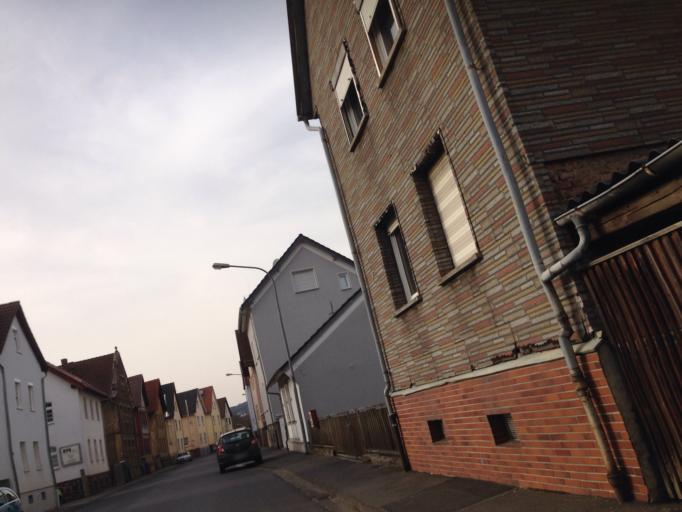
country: DE
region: Hesse
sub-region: Regierungsbezirk Giessen
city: Grossen Buseck
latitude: 50.6099
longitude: 8.7842
